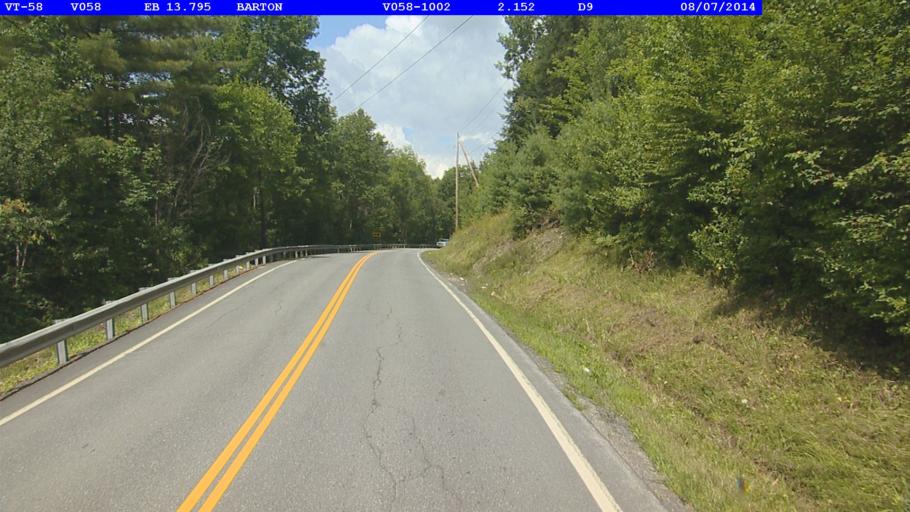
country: US
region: Vermont
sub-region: Orleans County
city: Newport
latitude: 44.8033
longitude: -72.1722
